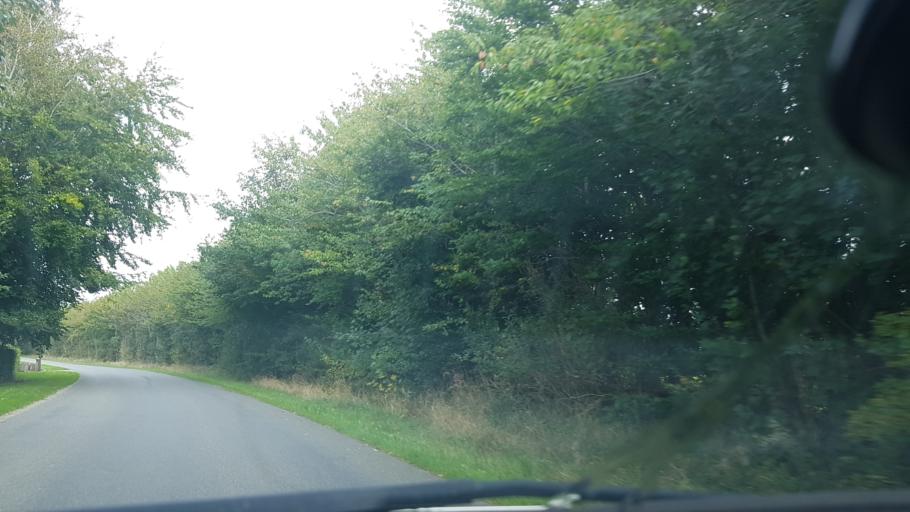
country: DK
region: South Denmark
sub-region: Vejen Kommune
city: Brorup
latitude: 55.4701
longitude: 8.9719
